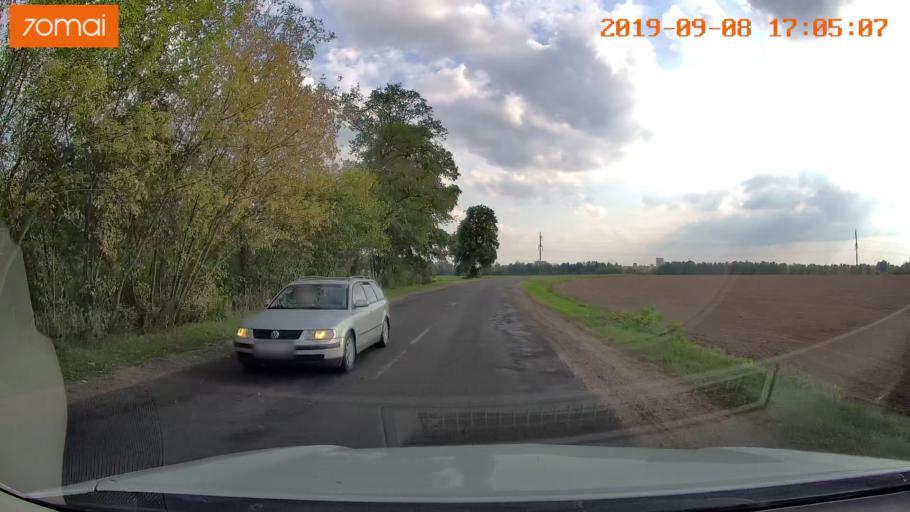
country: BY
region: Grodnenskaya
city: Hrodna
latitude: 53.6820
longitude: 23.9560
